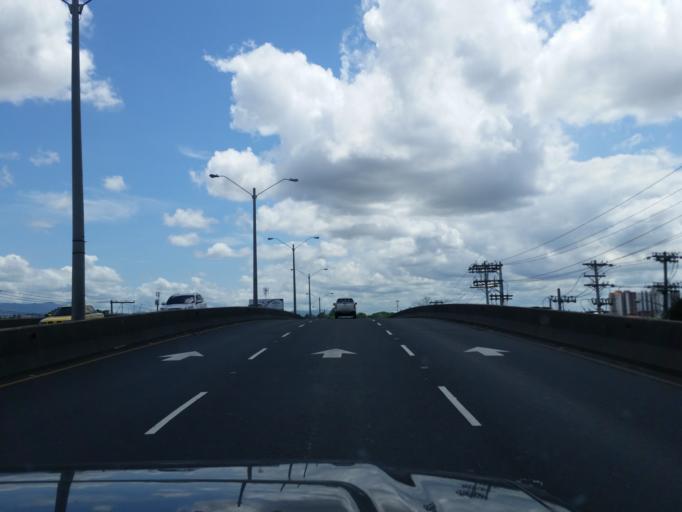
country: PA
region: Panama
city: San Miguelito
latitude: 9.0575
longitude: -79.4335
